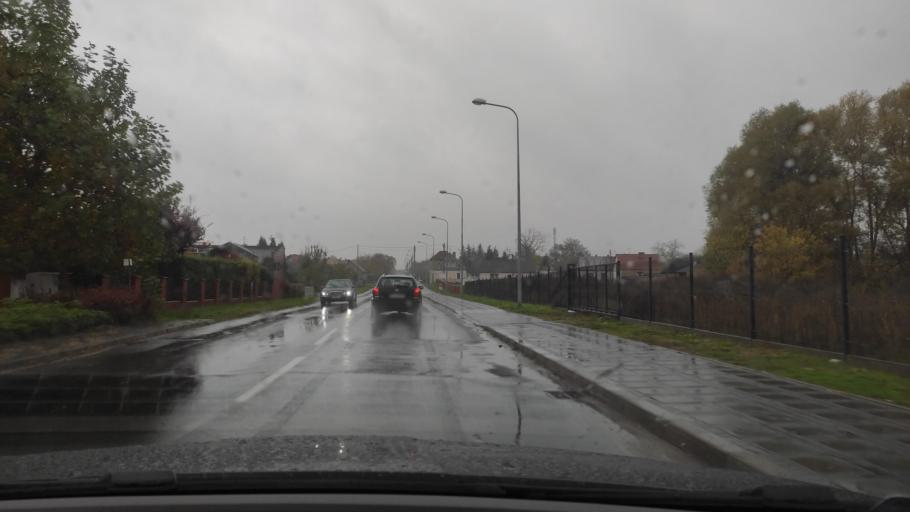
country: PL
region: Greater Poland Voivodeship
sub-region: Powiat poznanski
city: Kornik
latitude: 52.2299
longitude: 17.0943
